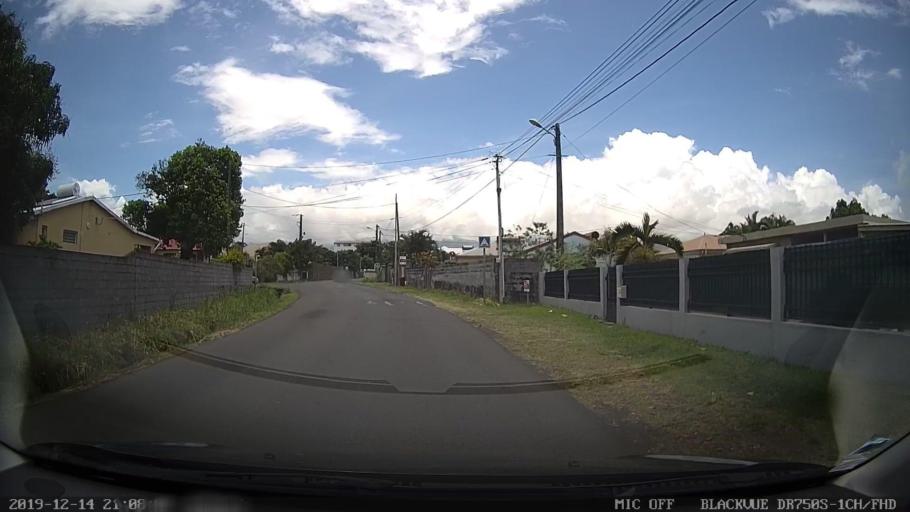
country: RE
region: Reunion
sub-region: Reunion
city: Saint-Andre
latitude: -20.9475
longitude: 55.6630
